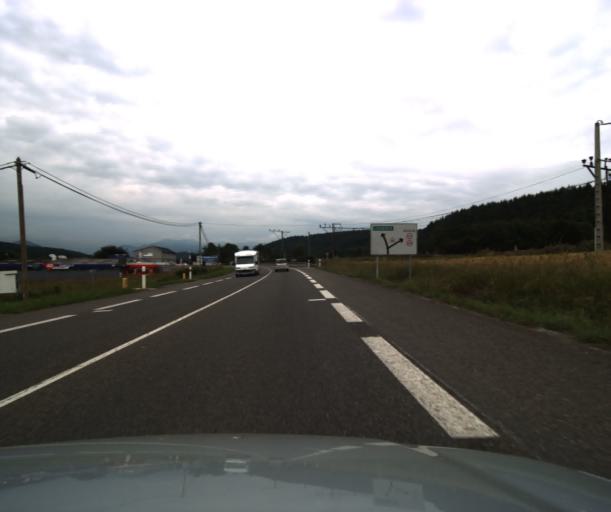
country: FR
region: Midi-Pyrenees
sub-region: Departement des Hautes-Pyrenees
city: Ossun
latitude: 43.1578
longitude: -0.0189
